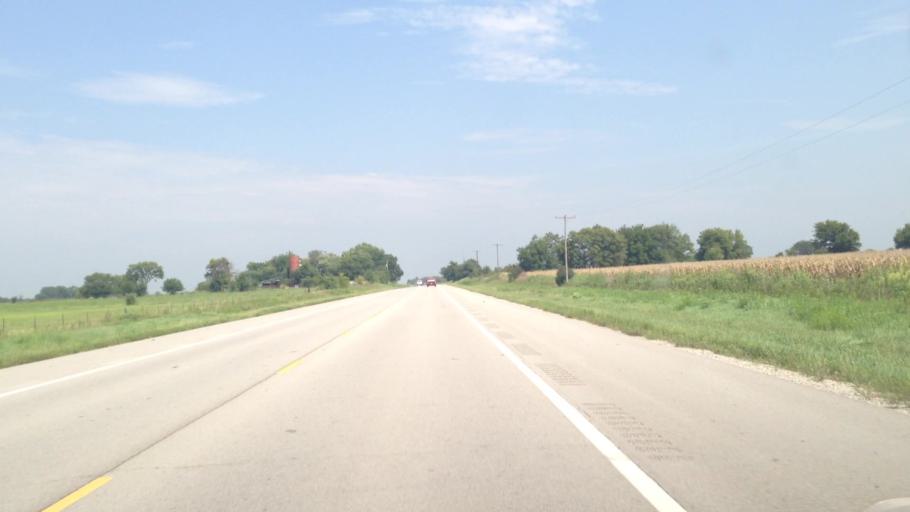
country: US
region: Kansas
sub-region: Labette County
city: Altamont
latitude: 37.2394
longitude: -95.2671
